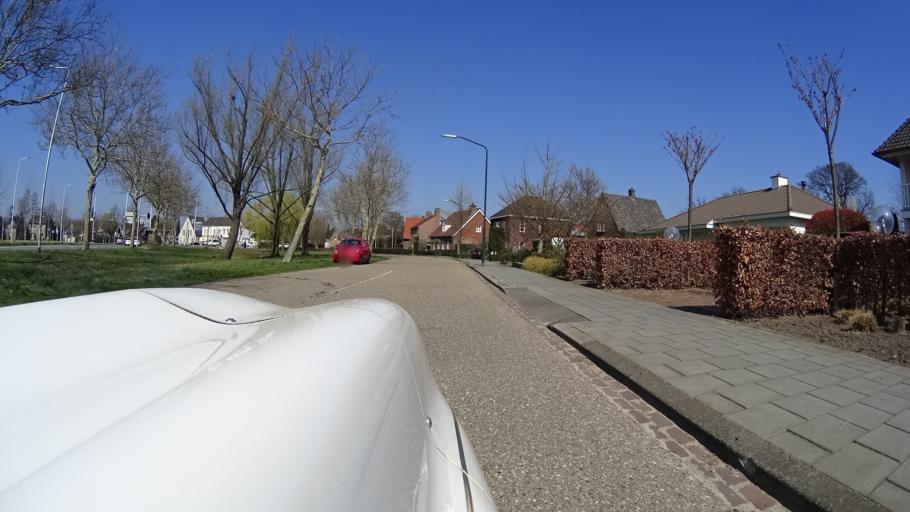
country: NL
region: North Brabant
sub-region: Gemeente Laarbeek
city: Aarle-Rixtel
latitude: 51.5274
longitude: 5.6414
